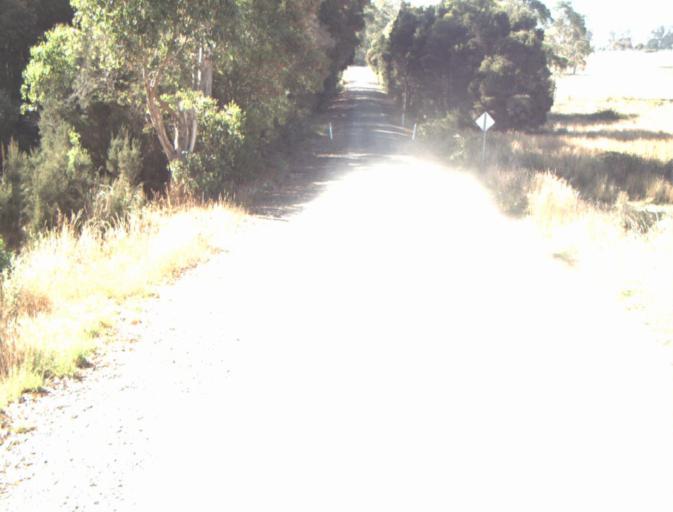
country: AU
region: Tasmania
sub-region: Dorset
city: Bridport
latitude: -41.1545
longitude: 147.2325
